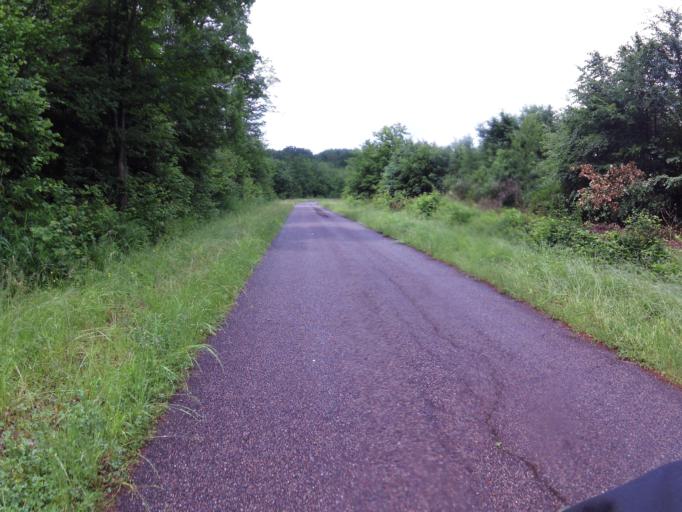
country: FR
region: Champagne-Ardenne
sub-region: Departement de la Marne
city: Sermaize-les-Bains
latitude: 48.7507
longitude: 4.9650
